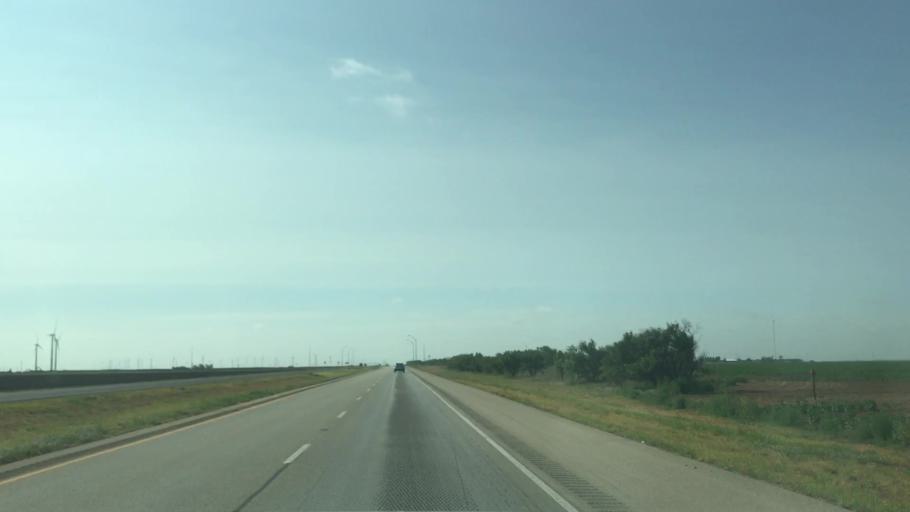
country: US
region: Texas
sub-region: Scurry County
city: Snyder
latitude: 32.6258
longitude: -100.7580
